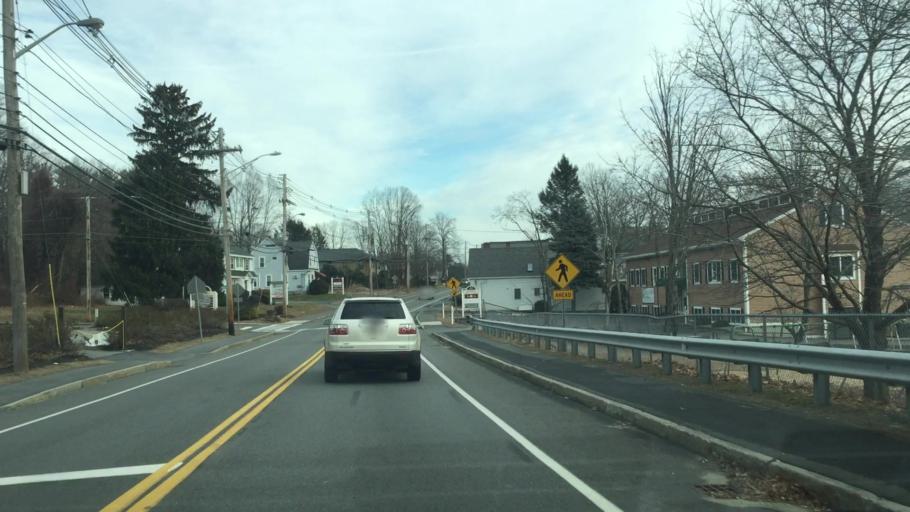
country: US
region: New Hampshire
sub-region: Rockingham County
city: Salem
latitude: 42.7823
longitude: -71.2368
